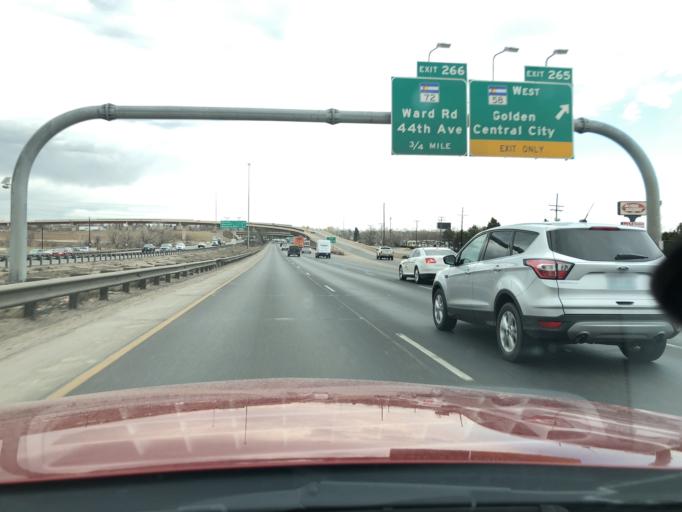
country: US
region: Colorado
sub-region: Jefferson County
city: Applewood
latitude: 39.7703
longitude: -105.1431
